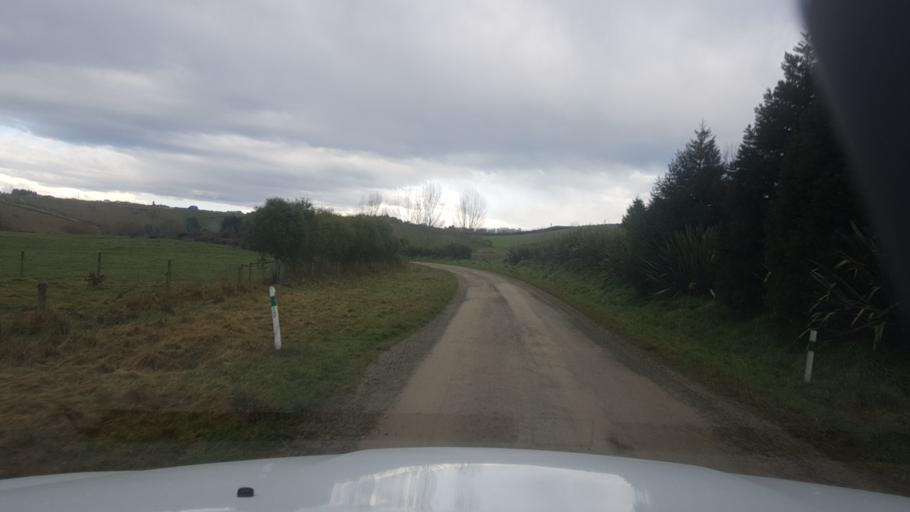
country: NZ
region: Canterbury
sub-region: Timaru District
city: Pleasant Point
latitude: -44.3419
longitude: 171.1624
